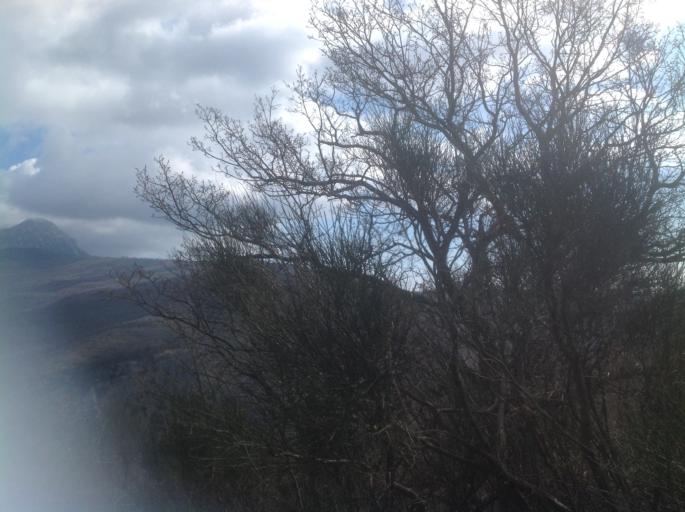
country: IT
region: Calabria
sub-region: Provincia di Cosenza
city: Civita
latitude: 39.8492
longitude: 16.3083
